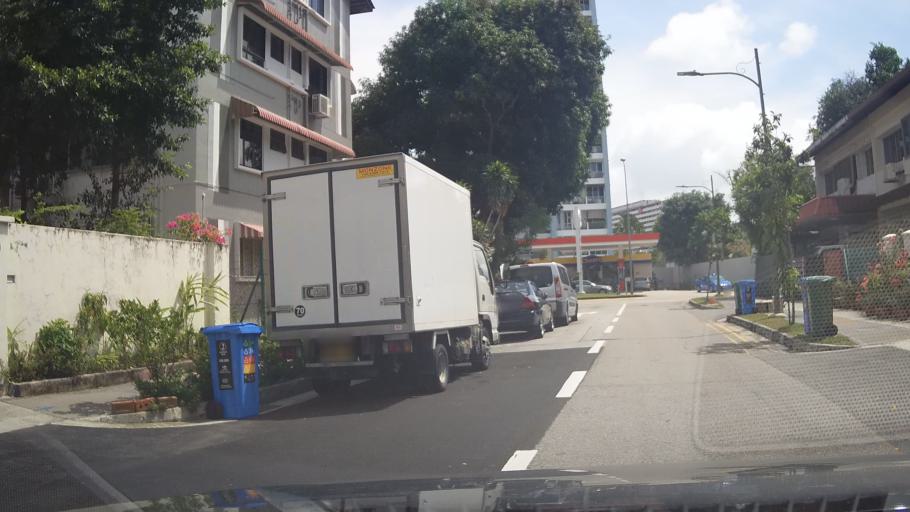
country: SG
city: Singapore
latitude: 1.3113
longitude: 103.8937
